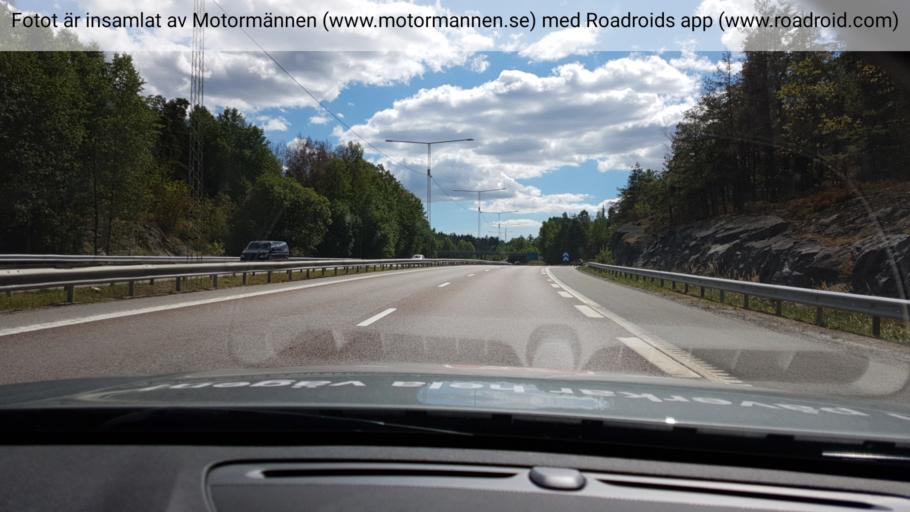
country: SE
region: Stockholm
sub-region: Nacka Kommun
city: Alta
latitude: 59.2548
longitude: 18.1699
